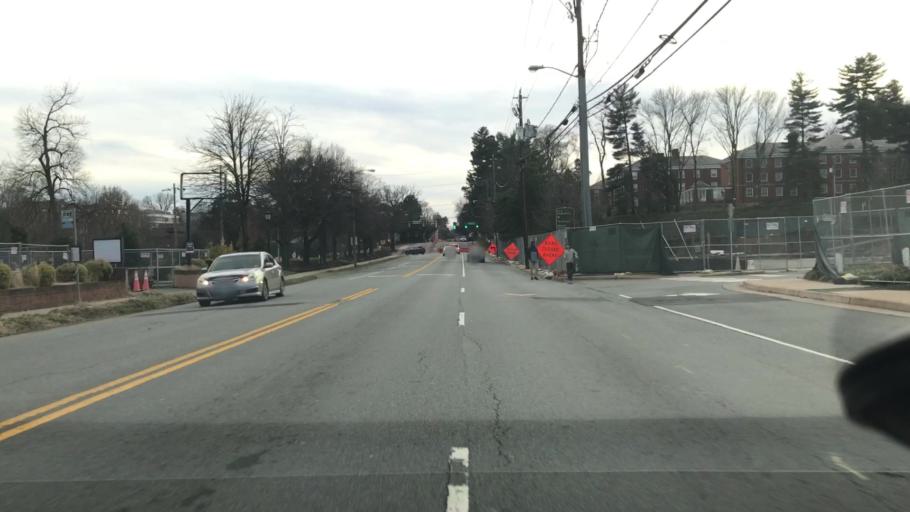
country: US
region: Virginia
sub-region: City of Charlottesville
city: Charlottesville
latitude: 38.0413
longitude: -78.5062
